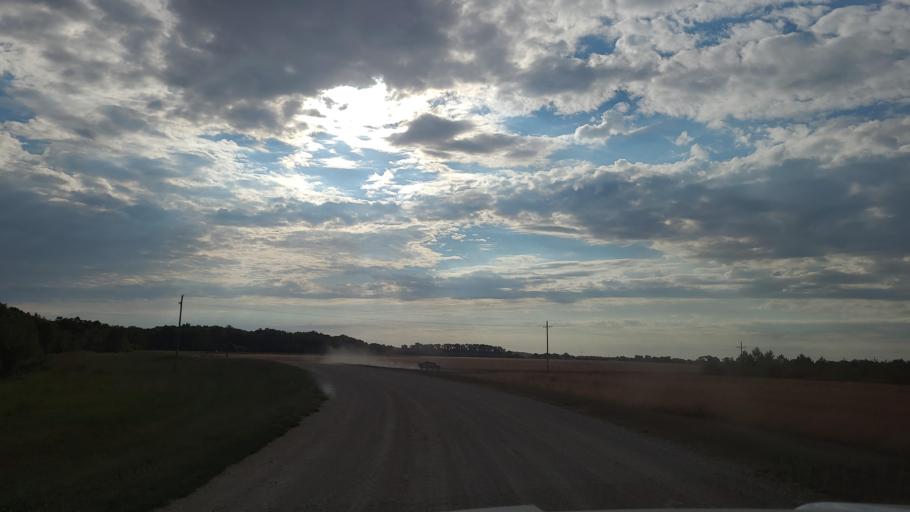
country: US
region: Kansas
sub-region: Douglas County
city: Lawrence
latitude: 39.0130
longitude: -95.2073
